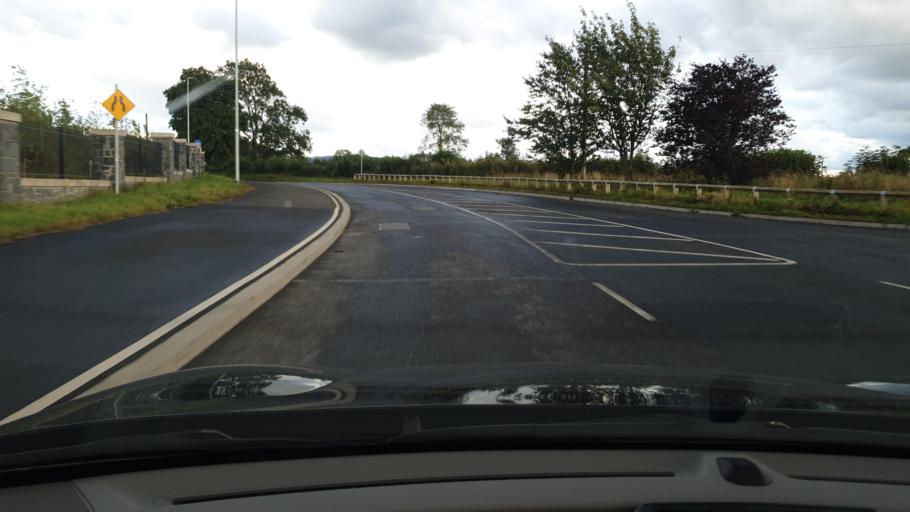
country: IE
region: Leinster
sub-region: South Dublin
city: Rathcoole
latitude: 53.3166
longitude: -6.4580
